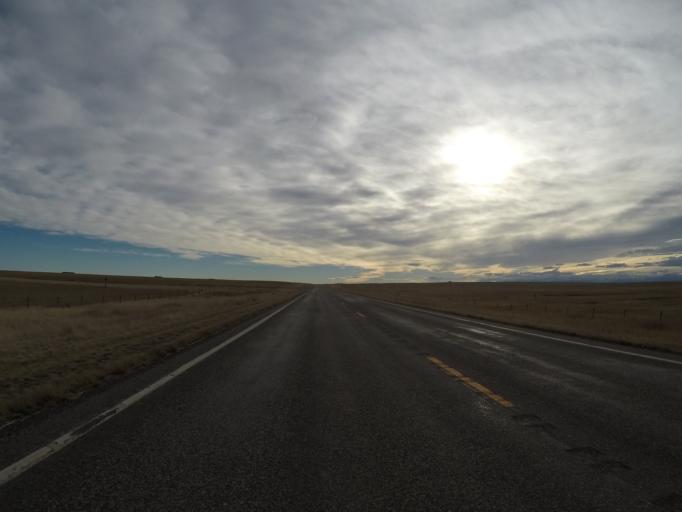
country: US
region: Montana
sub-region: Yellowstone County
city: Laurel
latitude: 45.8447
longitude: -108.8811
